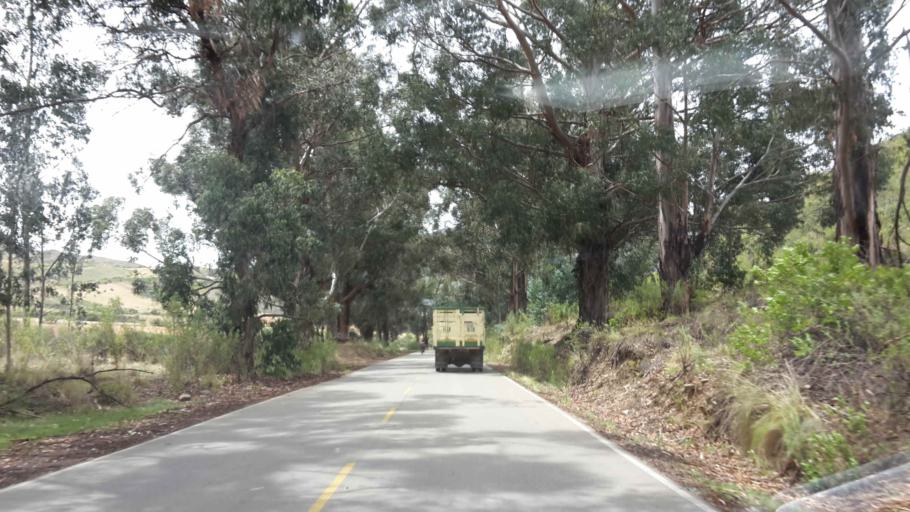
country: BO
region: Cochabamba
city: Totora
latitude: -17.6496
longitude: -65.2297
